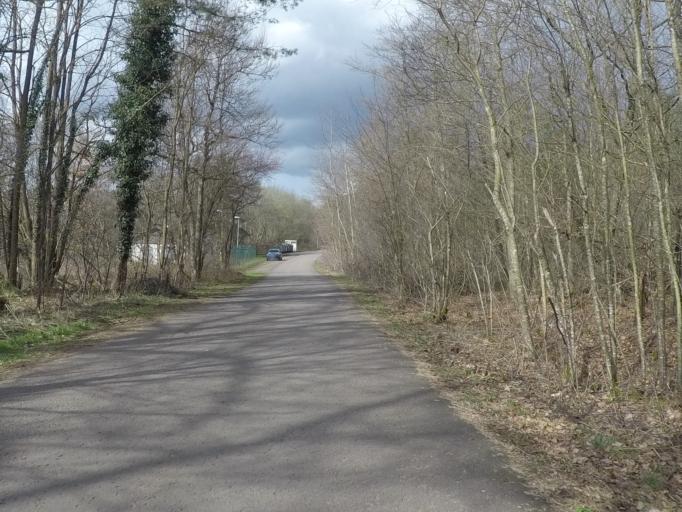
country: DE
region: Rheinland-Pfalz
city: Munchweiler an der Rodalbe
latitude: 49.2153
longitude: 7.7180
